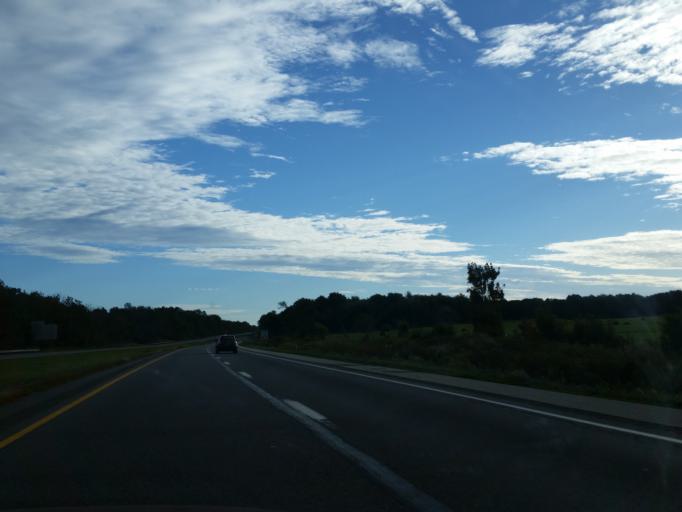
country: US
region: Pennsylvania
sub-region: Erie County
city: North East
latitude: 42.1594
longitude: -79.8795
